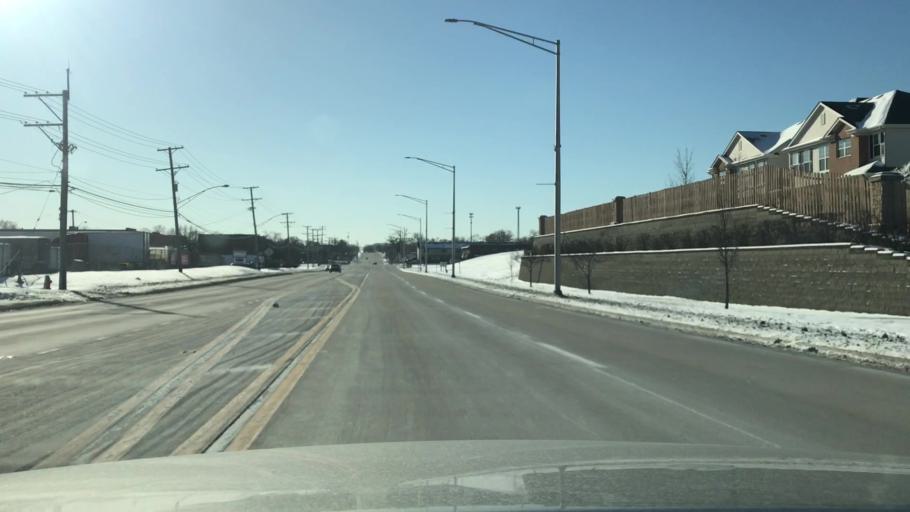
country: US
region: Illinois
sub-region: Cook County
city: Justice
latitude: 41.7426
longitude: -87.8384
